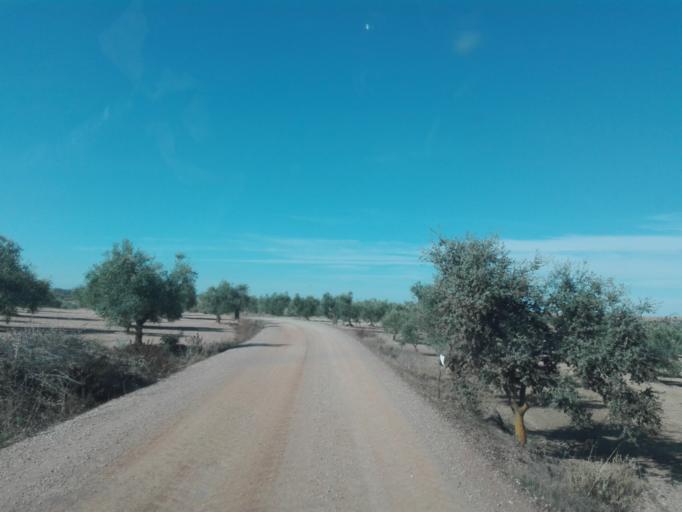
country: ES
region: Extremadura
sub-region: Provincia de Badajoz
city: Ahillones
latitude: 38.2828
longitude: -5.9055
